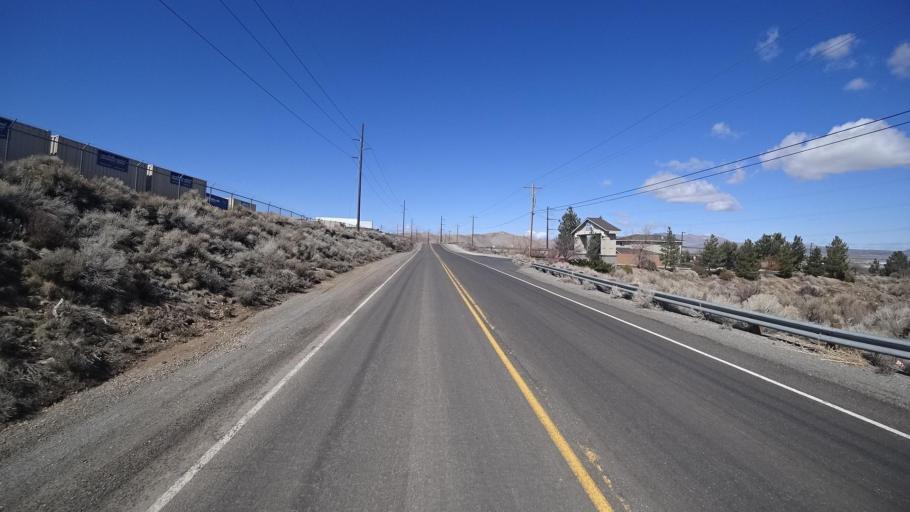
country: US
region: Nevada
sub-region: Washoe County
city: Lemmon Valley
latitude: 39.6188
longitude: -119.8897
